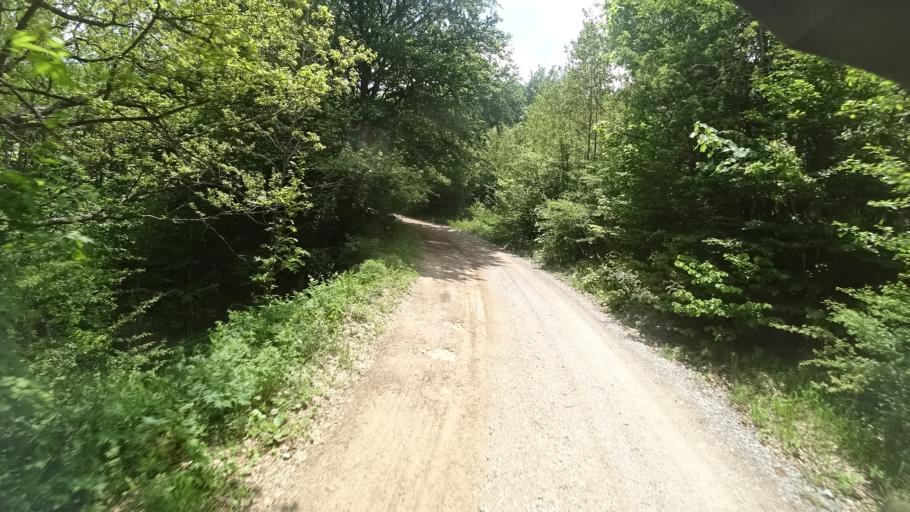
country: HR
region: Zadarska
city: Gracac
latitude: 44.5001
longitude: 15.8771
